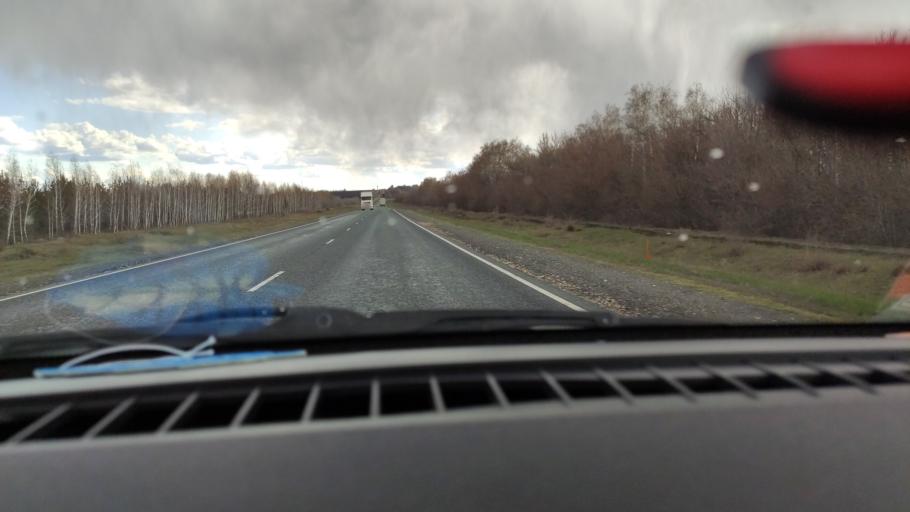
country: RU
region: Saratov
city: Balakovo
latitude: 52.1416
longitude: 47.8017
